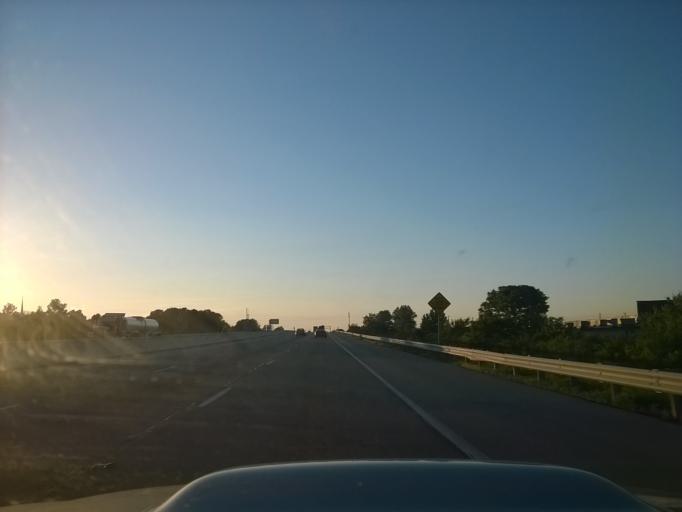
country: US
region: Indiana
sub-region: Marion County
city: Speedway
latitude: 39.8504
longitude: -86.2630
